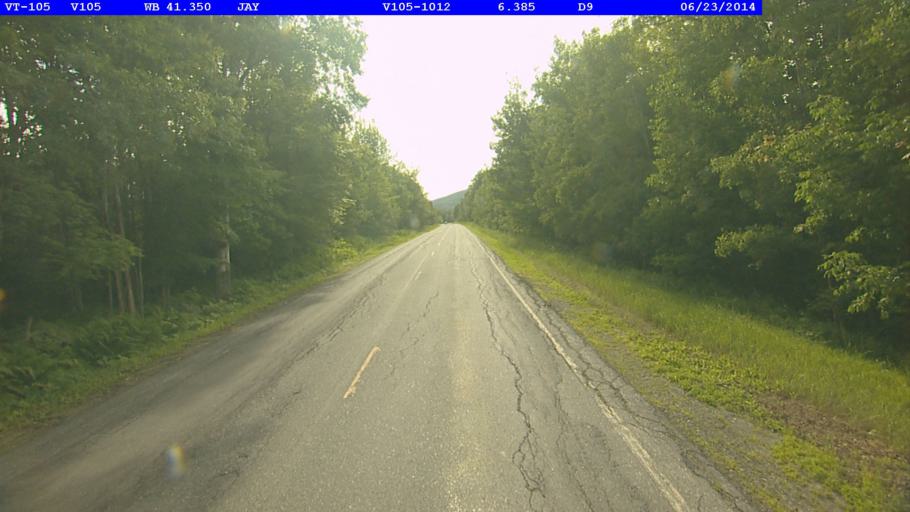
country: CA
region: Quebec
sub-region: Monteregie
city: Sutton
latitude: 44.9727
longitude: -72.4600
